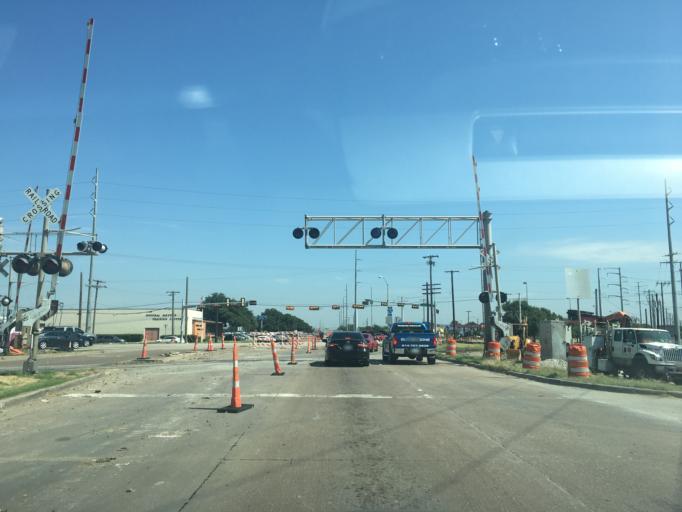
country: US
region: Texas
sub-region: Dallas County
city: Garland
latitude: 32.8707
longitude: -96.6655
